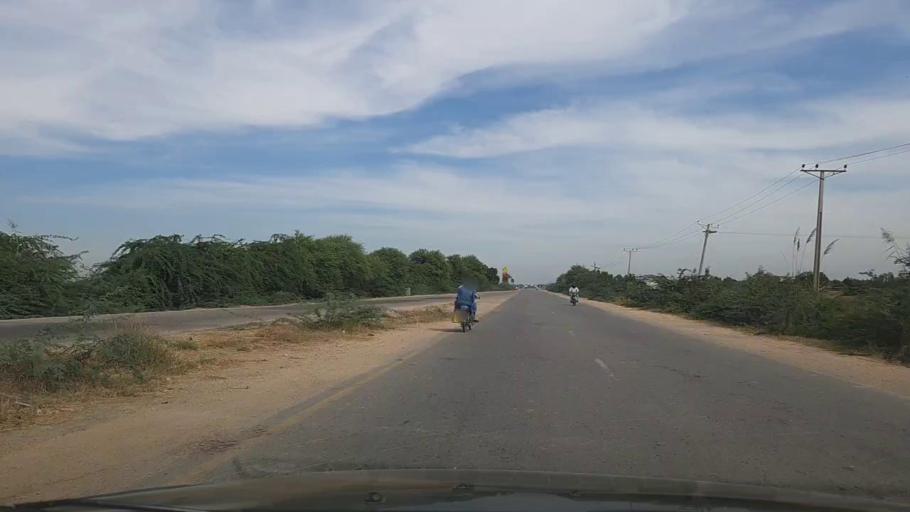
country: PK
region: Sindh
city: Thatta
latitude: 24.7667
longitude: 67.9373
